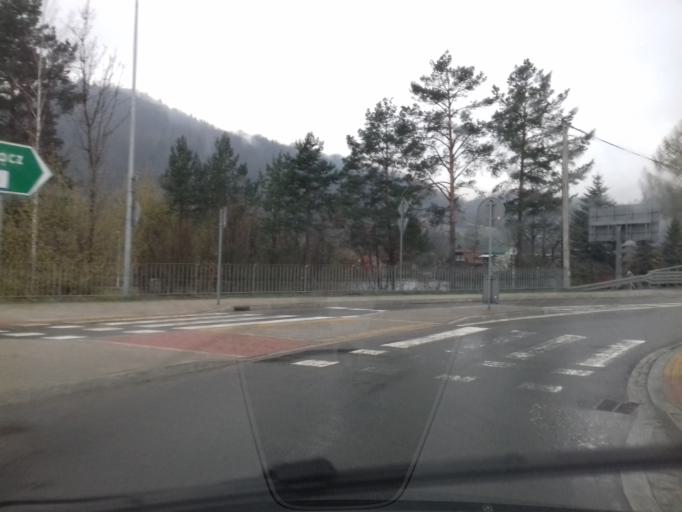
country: PL
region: Lesser Poland Voivodeship
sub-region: Powiat nowosadecki
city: Piwniczna-Zdroj
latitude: 49.4201
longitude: 20.7259
